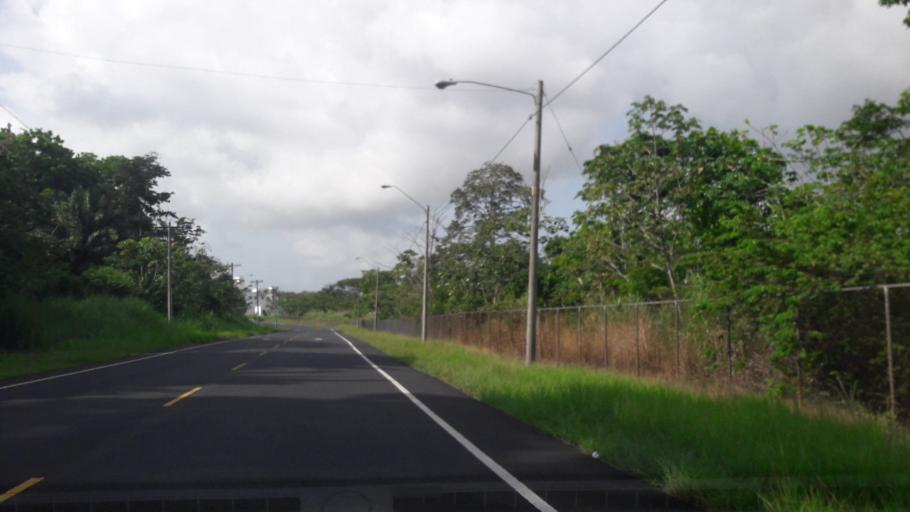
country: PA
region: Colon
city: Cativa
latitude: 9.3562
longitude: -79.8632
